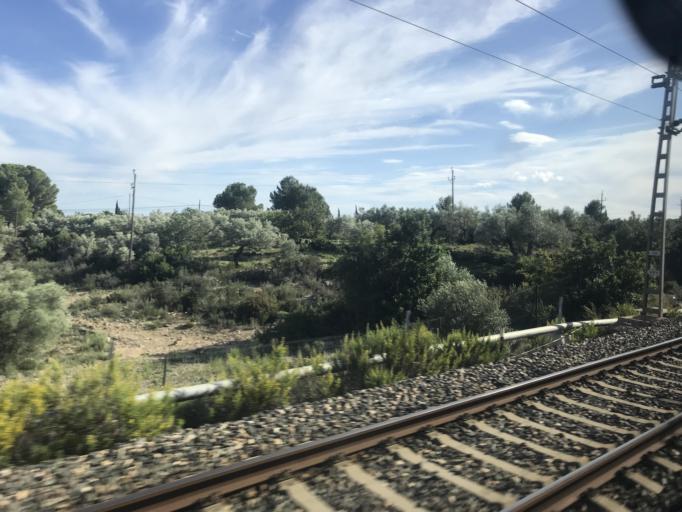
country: ES
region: Catalonia
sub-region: Provincia de Tarragona
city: l'Ametlla de Mar
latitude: 40.8966
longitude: 0.8107
